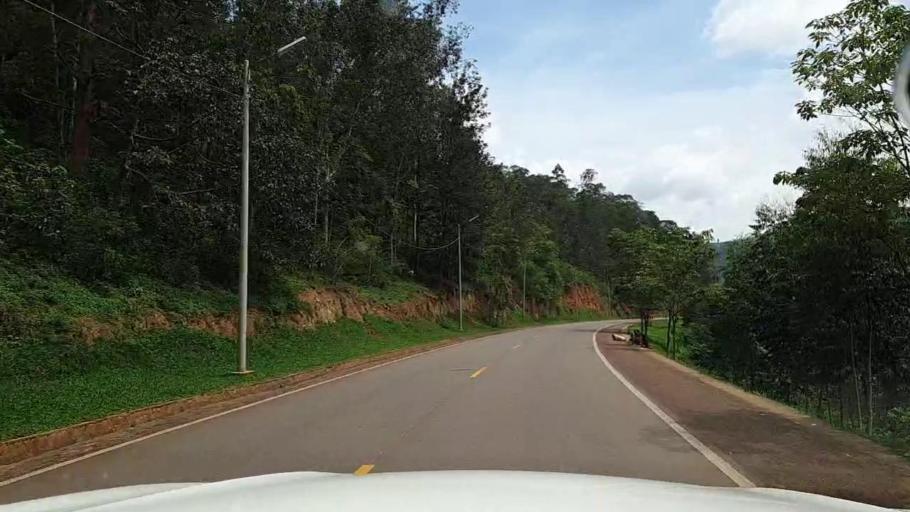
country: RW
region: Kigali
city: Kigali
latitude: -1.8604
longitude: 30.0906
